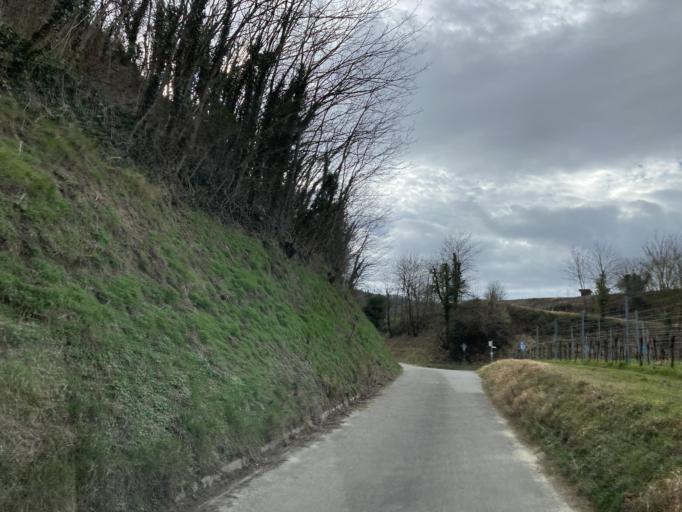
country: DE
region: Baden-Wuerttemberg
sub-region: Freiburg Region
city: Endingen
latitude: 48.1328
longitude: 7.7028
